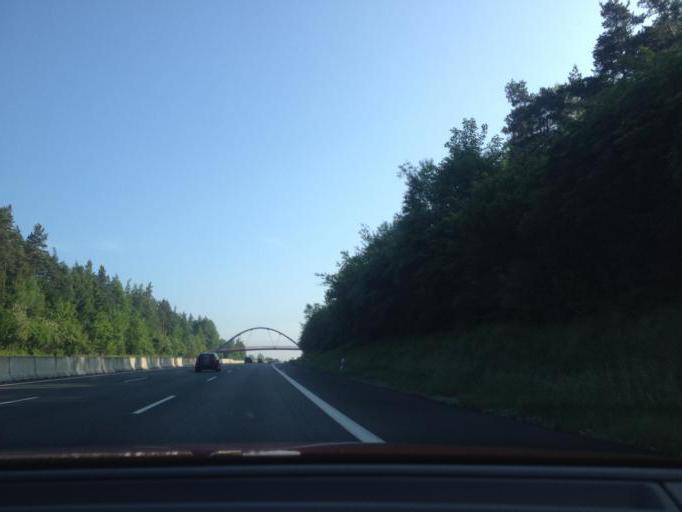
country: DE
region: Bavaria
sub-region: Regierungsbezirk Mittelfranken
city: Schnaittach
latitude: 49.5573
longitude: 11.3244
